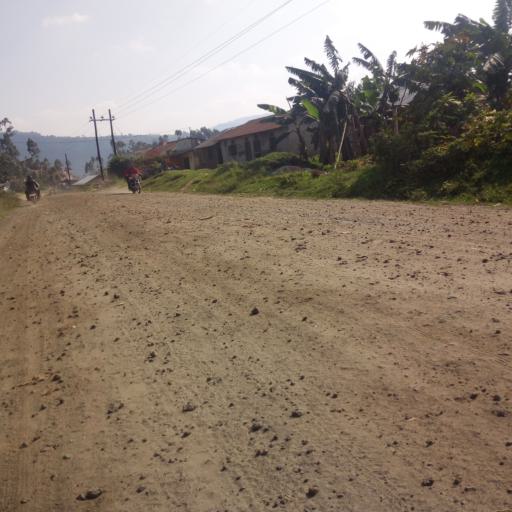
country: UG
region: Western Region
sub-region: Kisoro District
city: Kisoro
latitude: -1.2312
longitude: 29.7111
